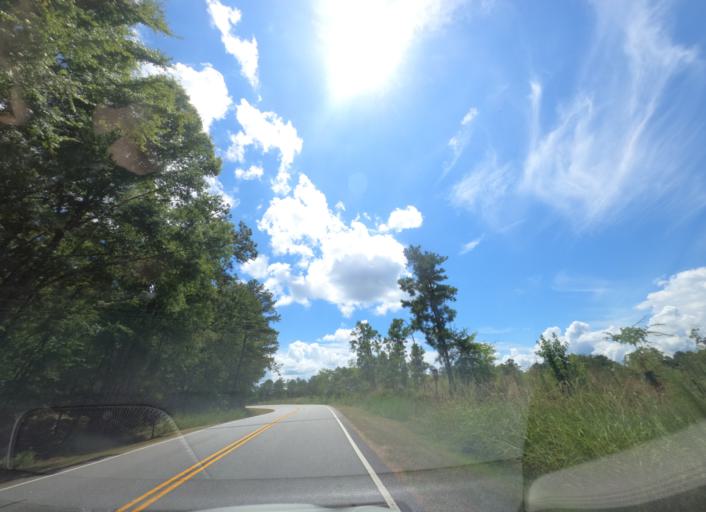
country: US
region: Georgia
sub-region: Lincoln County
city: Lincolnton
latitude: 33.8824
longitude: -82.4127
